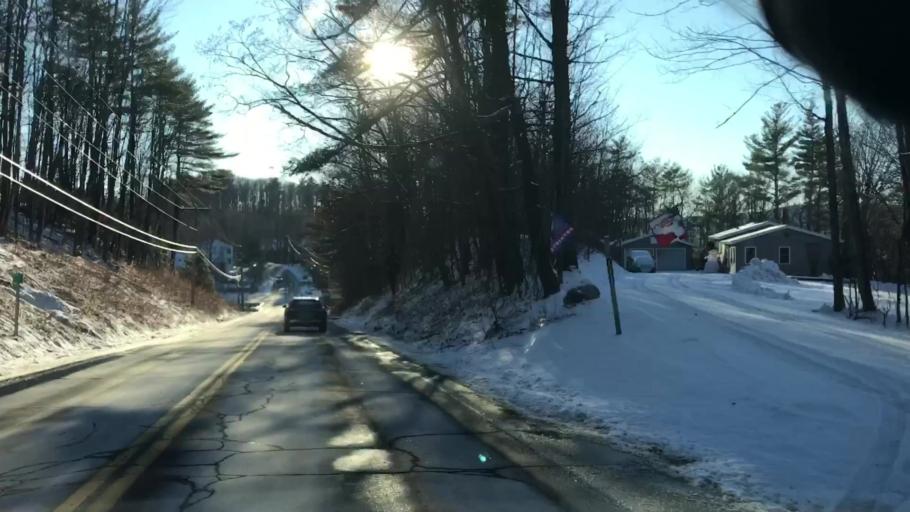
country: US
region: New Hampshire
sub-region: Grafton County
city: Haverhill
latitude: 44.0447
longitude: -72.0563
